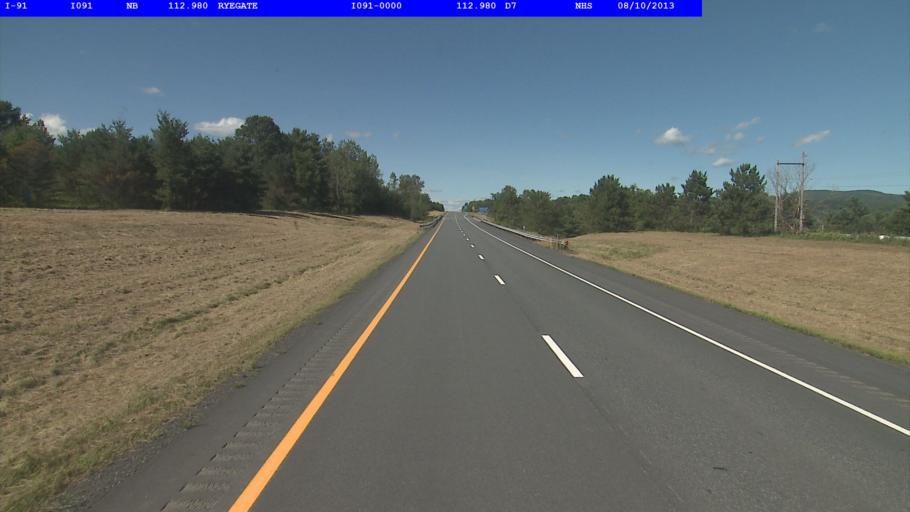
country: US
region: New Hampshire
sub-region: Grafton County
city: Woodsville
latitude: 44.1959
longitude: -72.0717
